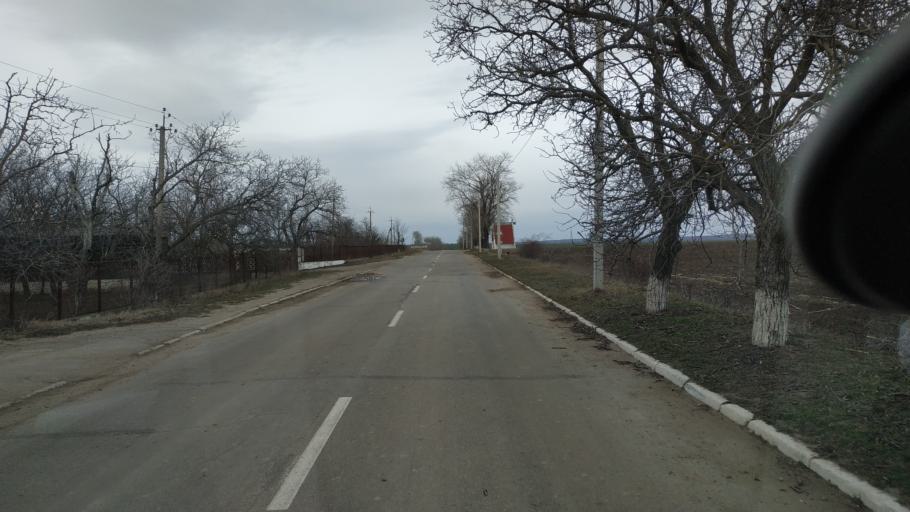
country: MD
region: Telenesti
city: Cocieri
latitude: 47.3555
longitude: 29.1164
